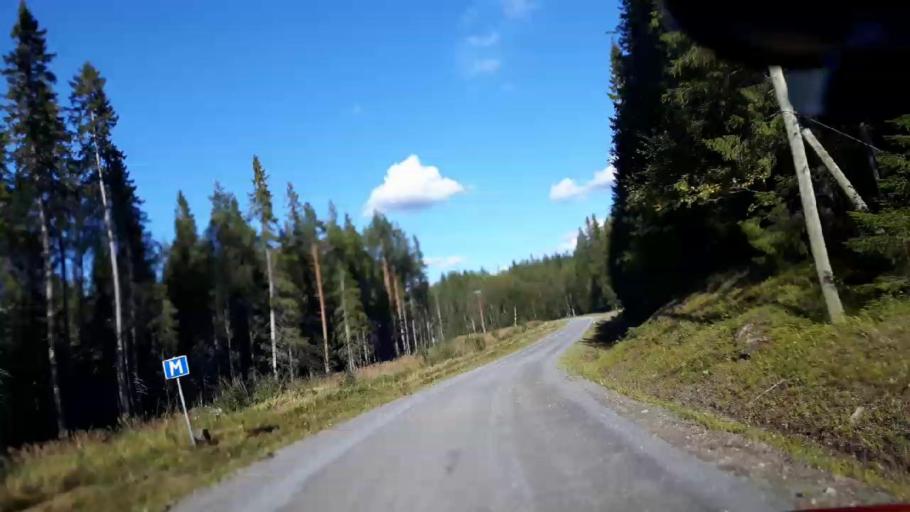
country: SE
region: Jaemtland
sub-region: Ragunda Kommun
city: Hammarstrand
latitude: 63.5138
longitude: 16.0513
